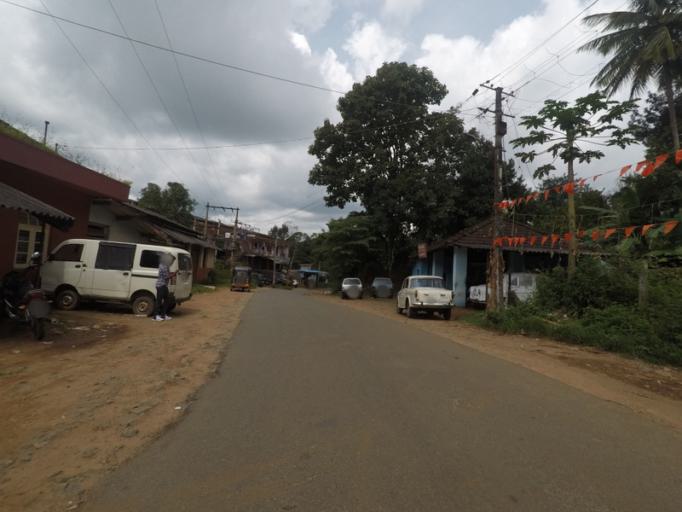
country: IN
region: Karnataka
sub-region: Kodagu
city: Virarajendrapet
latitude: 12.2949
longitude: 75.8749
